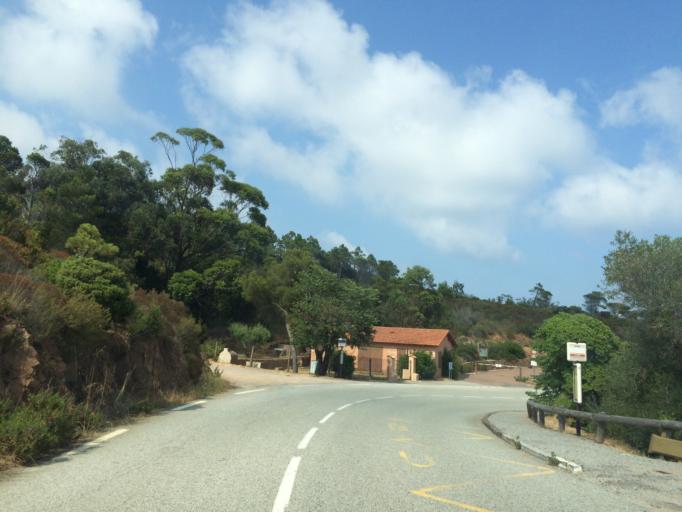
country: FR
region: Provence-Alpes-Cote d'Azur
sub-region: Departement des Alpes-Maritimes
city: Theoule-sur-Mer
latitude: 43.4496
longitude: 6.9158
